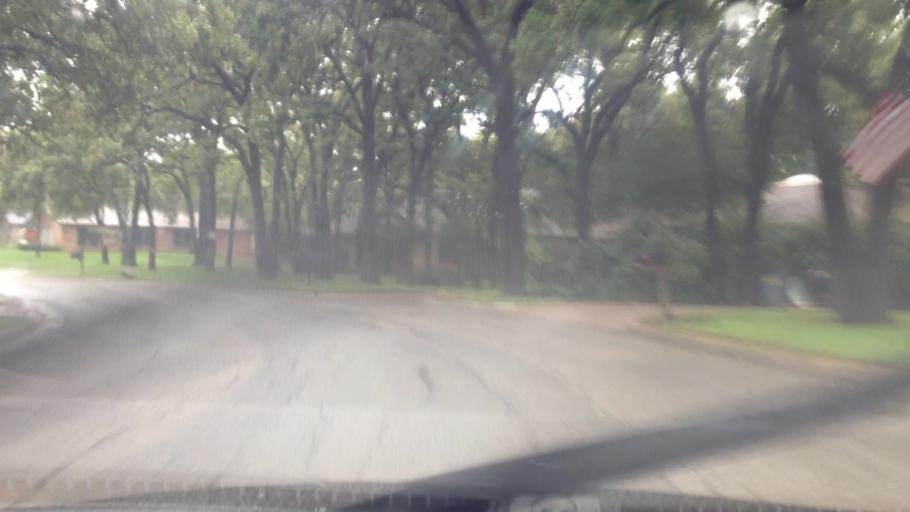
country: US
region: Texas
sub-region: Tarrant County
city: Watauga
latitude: 32.8784
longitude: -97.2181
